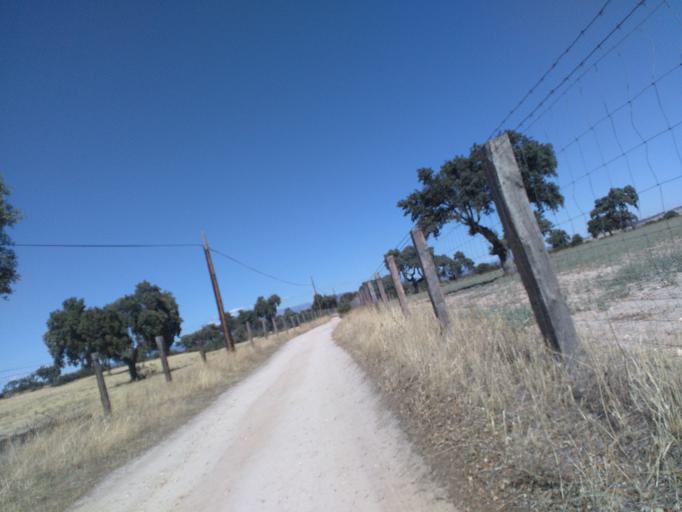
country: ES
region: Madrid
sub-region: Provincia de Madrid
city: Villanueva del Pardillo
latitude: 40.4564
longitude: -3.9564
